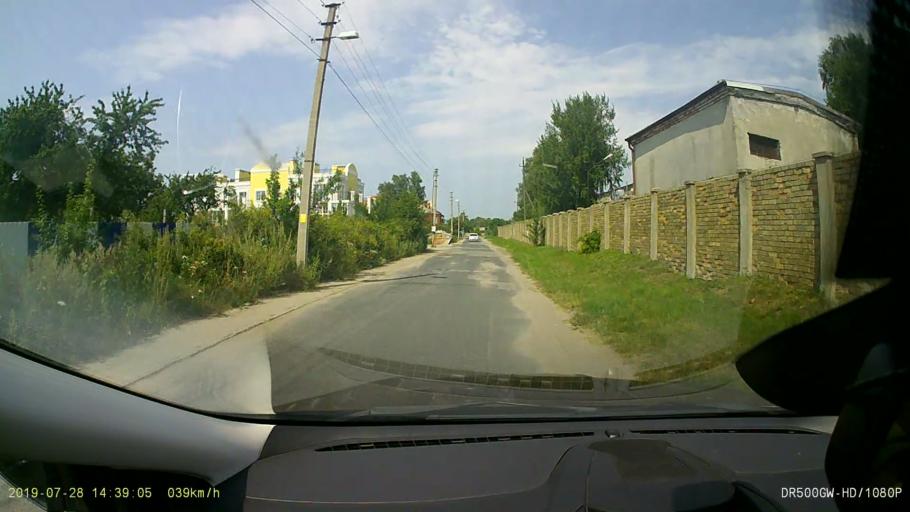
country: RU
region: Kaliningrad
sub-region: Gorod Kaliningrad
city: Yantarnyy
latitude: 54.8741
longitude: 19.9395
